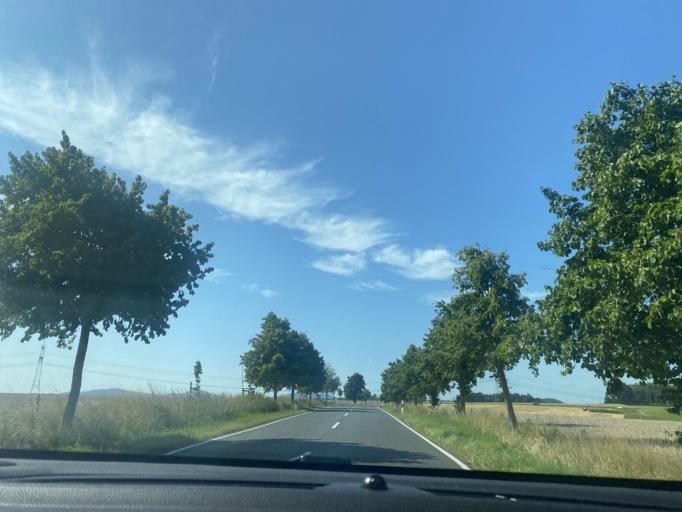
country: DE
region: Saxony
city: Bernstadt
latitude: 51.0363
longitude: 14.8154
